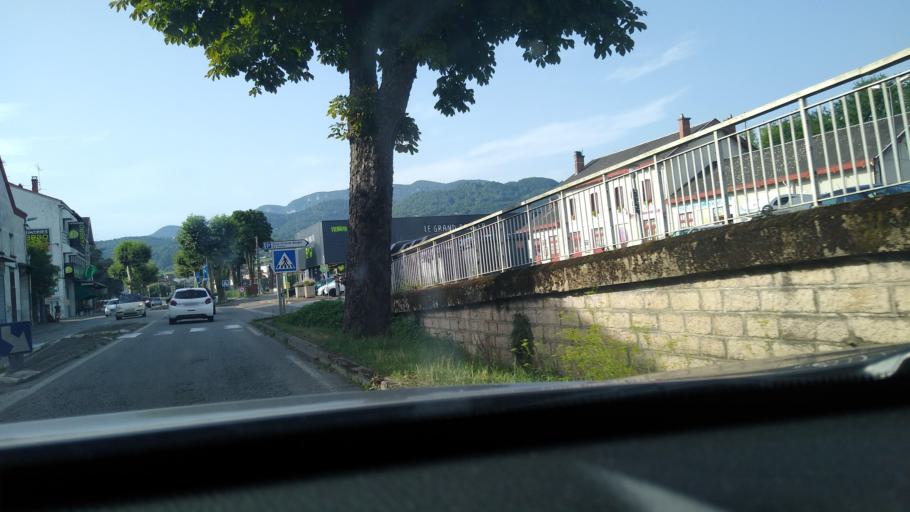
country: FR
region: Midi-Pyrenees
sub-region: Departement de l'Ariege
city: Saint-Girons
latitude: 42.9888
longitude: 1.1394
